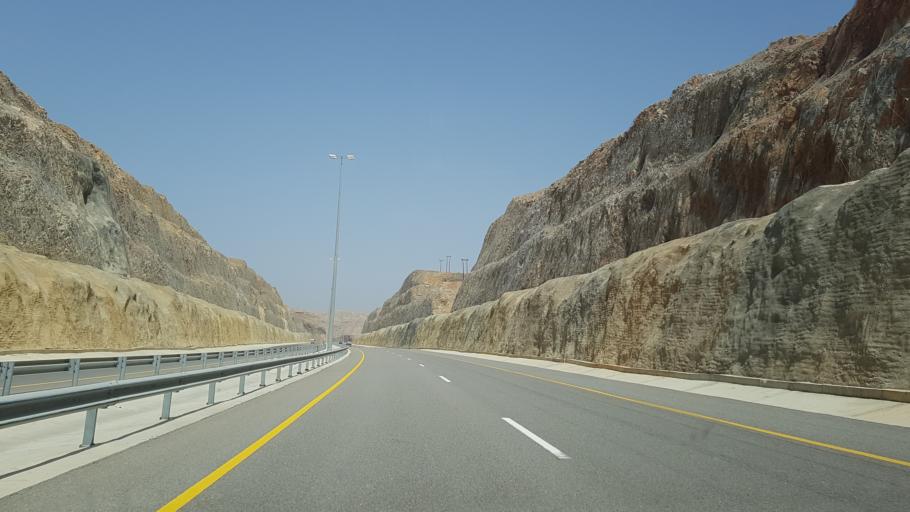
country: OM
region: Muhafazat Masqat
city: Muscat
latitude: 23.1884
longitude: 58.8614
